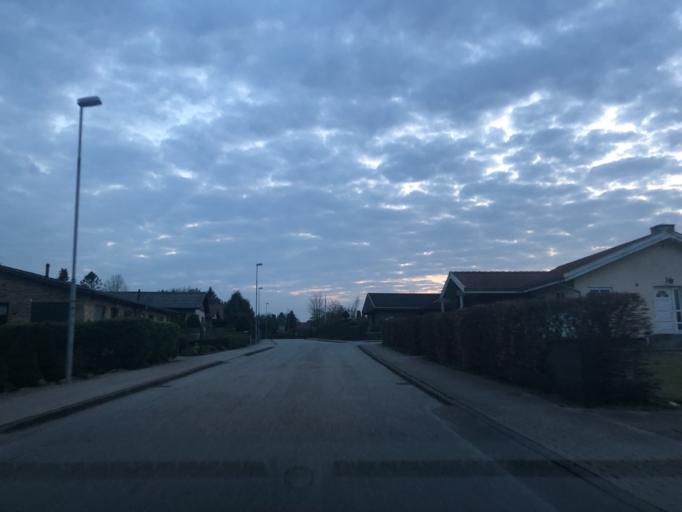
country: DK
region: Zealand
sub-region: Ringsted Kommune
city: Ringsted
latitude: 55.4384
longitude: 11.7756
